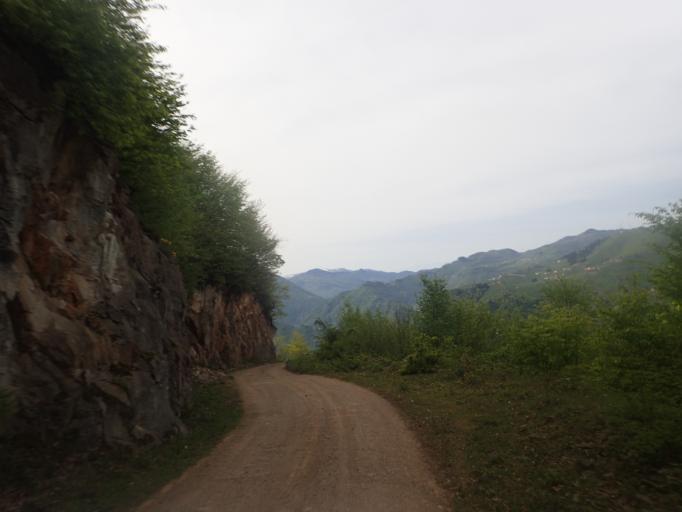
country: TR
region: Ordu
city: Kabaduz
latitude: 40.8088
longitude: 37.8749
